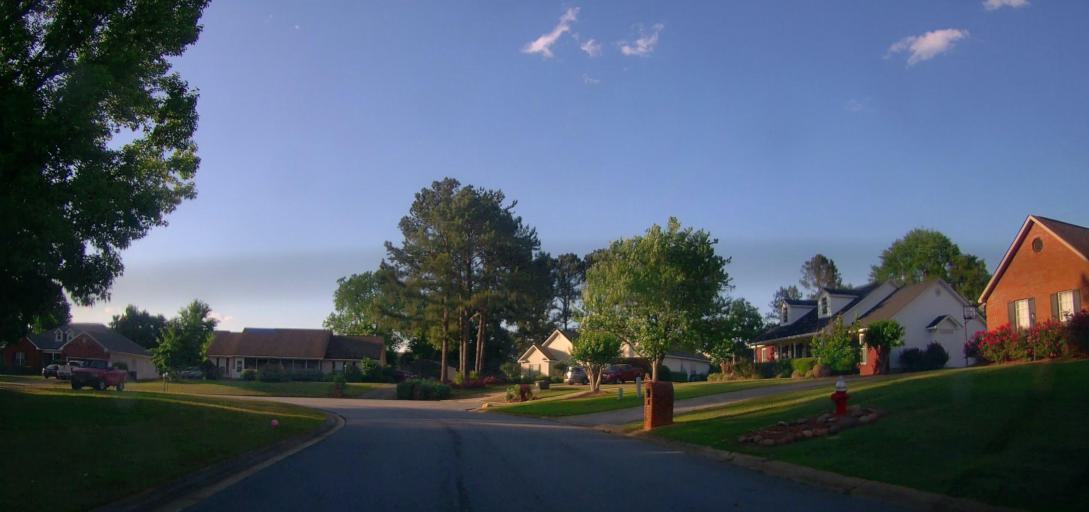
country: US
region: Georgia
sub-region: Houston County
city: Centerville
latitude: 32.6424
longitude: -83.7142
